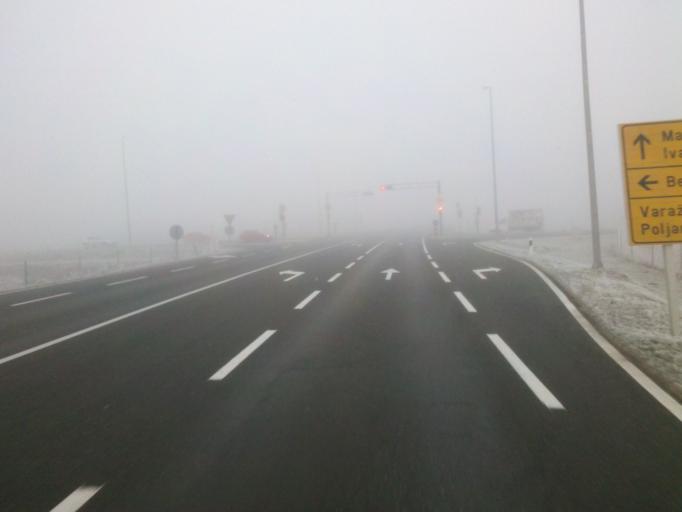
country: HR
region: Varazdinska
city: Jalkovec
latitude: 46.2631
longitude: 16.3145
